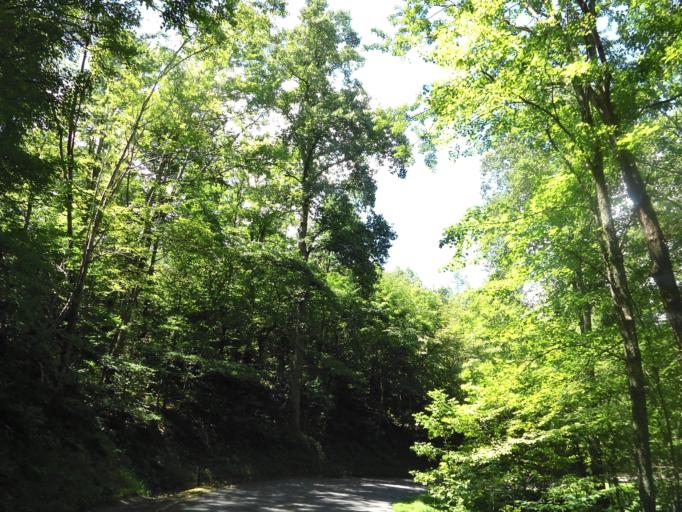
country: US
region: Tennessee
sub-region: Claiborne County
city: Harrogate
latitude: 36.6103
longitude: -83.6713
